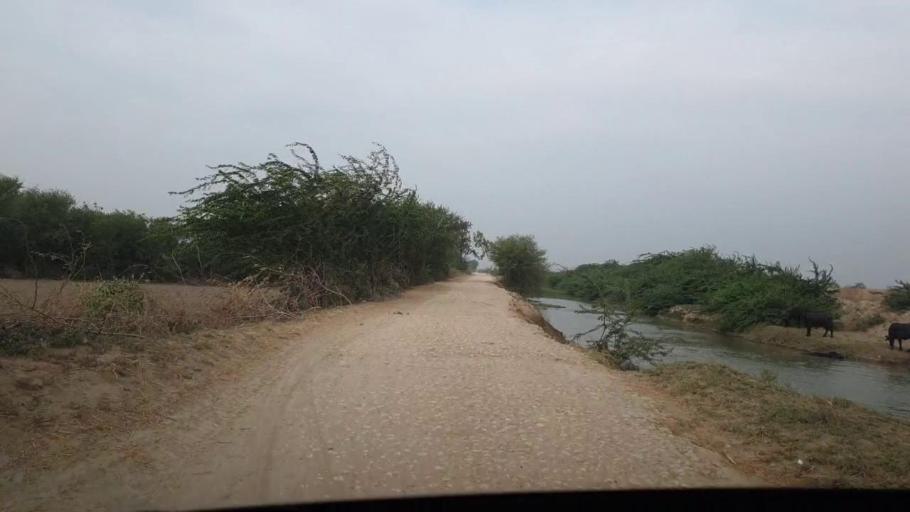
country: PK
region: Sindh
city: Chuhar Jamali
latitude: 24.4117
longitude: 67.9454
